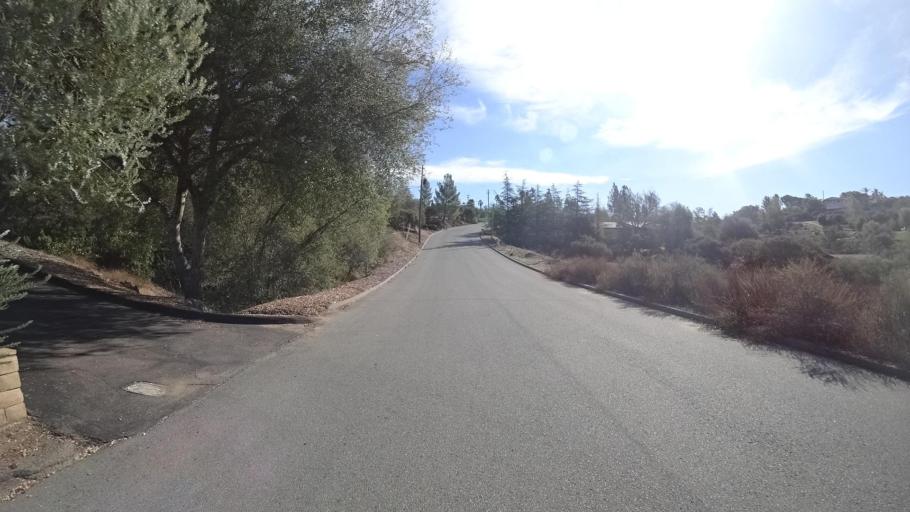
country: US
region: California
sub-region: San Diego County
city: Alpine
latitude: 32.8149
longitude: -116.7346
